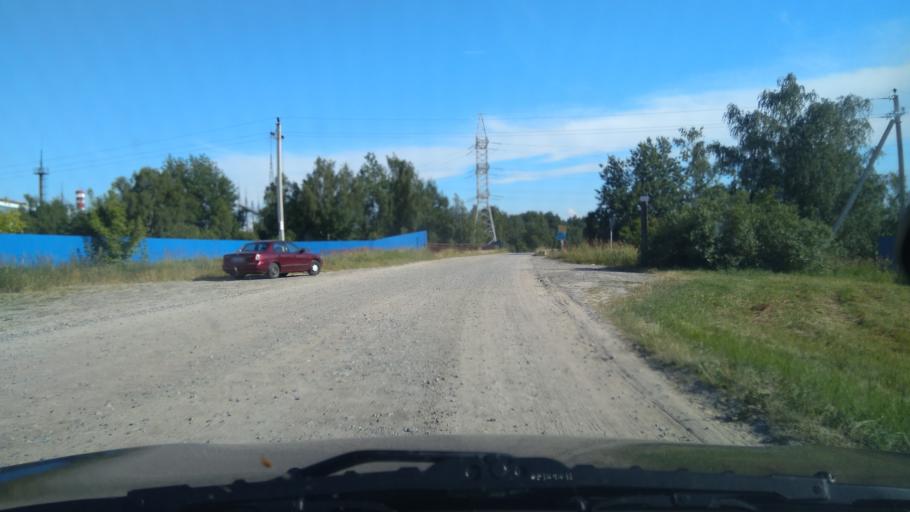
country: BY
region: Brest
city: Byelaazyorsk
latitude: 52.4561
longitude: 25.1868
